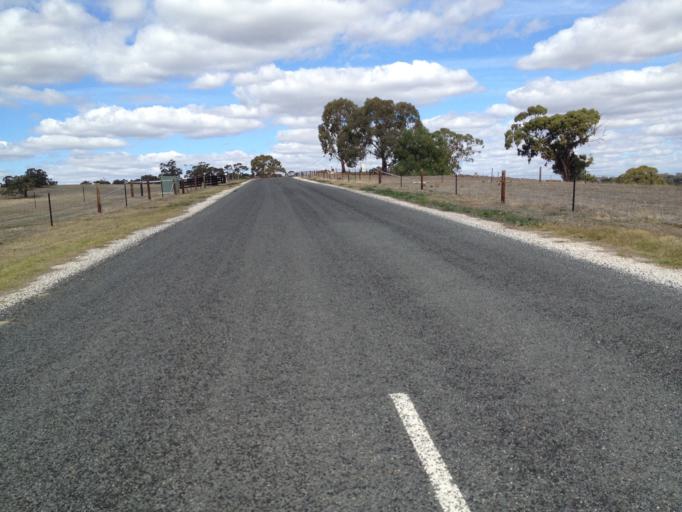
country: AU
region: South Australia
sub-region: Barossa
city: Lyndoch
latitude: -34.6300
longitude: 138.8308
